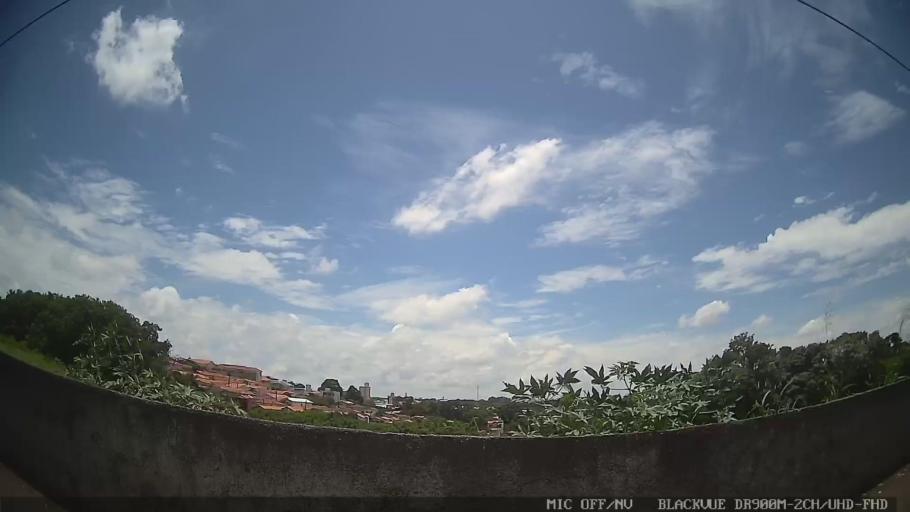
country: BR
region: Sao Paulo
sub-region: Laranjal Paulista
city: Laranjal Paulista
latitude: -23.0526
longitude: -47.8320
